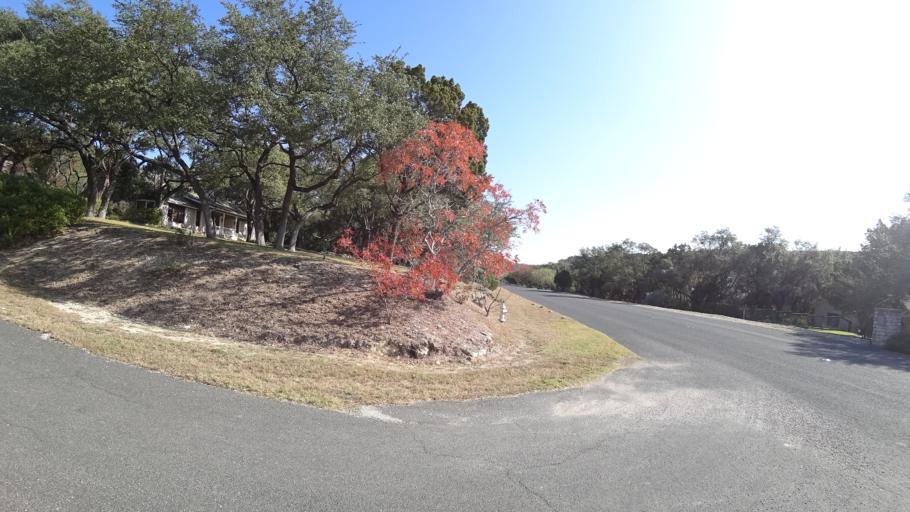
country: US
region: Texas
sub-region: Travis County
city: West Lake Hills
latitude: 30.3713
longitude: -97.8178
